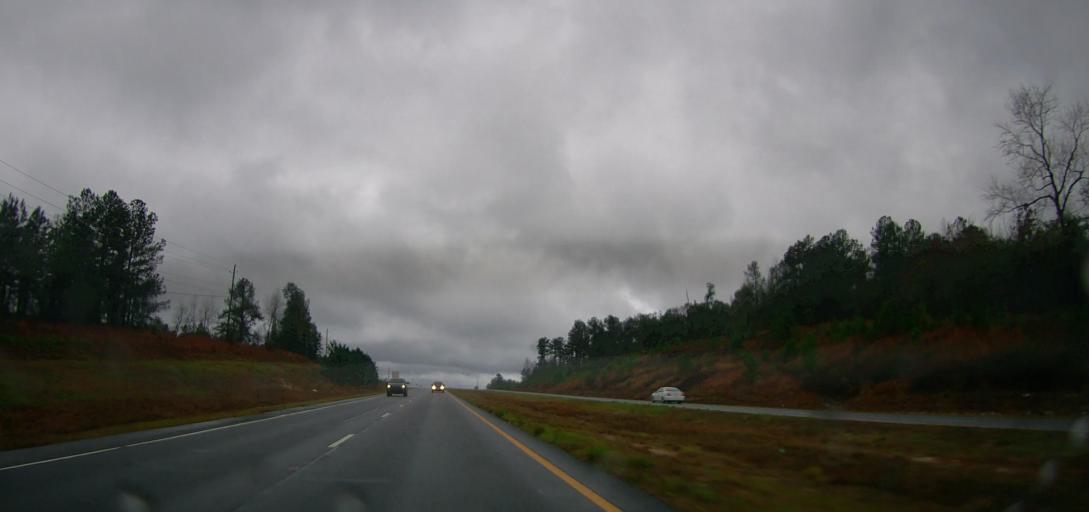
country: US
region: Georgia
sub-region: Jackson County
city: Commerce
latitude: 34.1770
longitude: -83.4434
